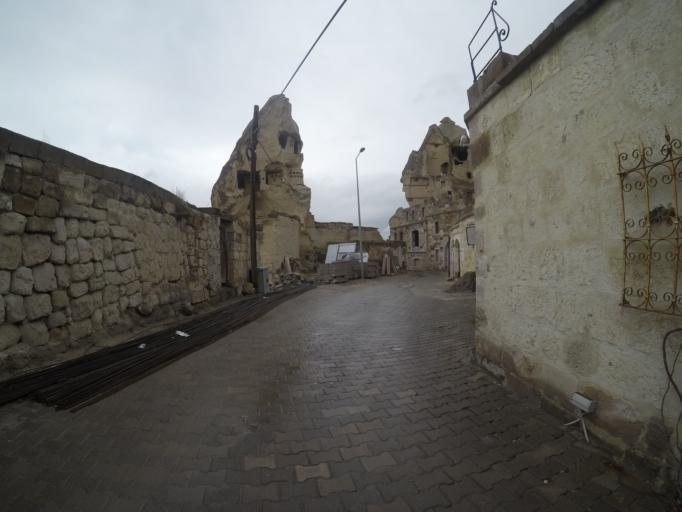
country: TR
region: Nevsehir
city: Goereme
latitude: 38.6409
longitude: 34.8312
